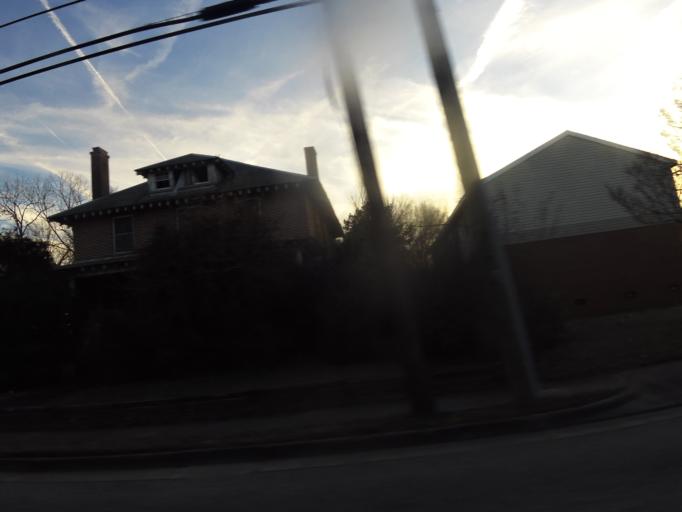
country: US
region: Virginia
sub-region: City of Franklin
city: Franklin
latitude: 36.6793
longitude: -76.9305
